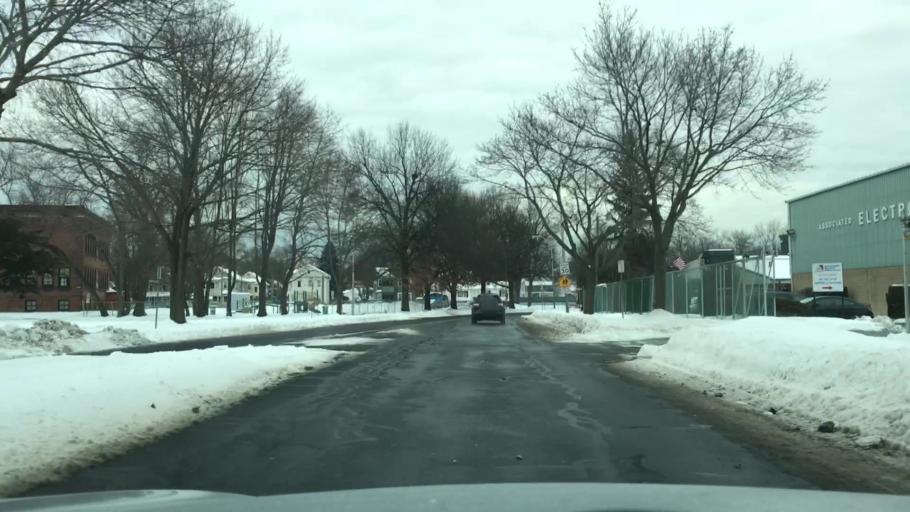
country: US
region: Massachusetts
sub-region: Hampden County
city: West Springfield
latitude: 42.1190
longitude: -72.6138
